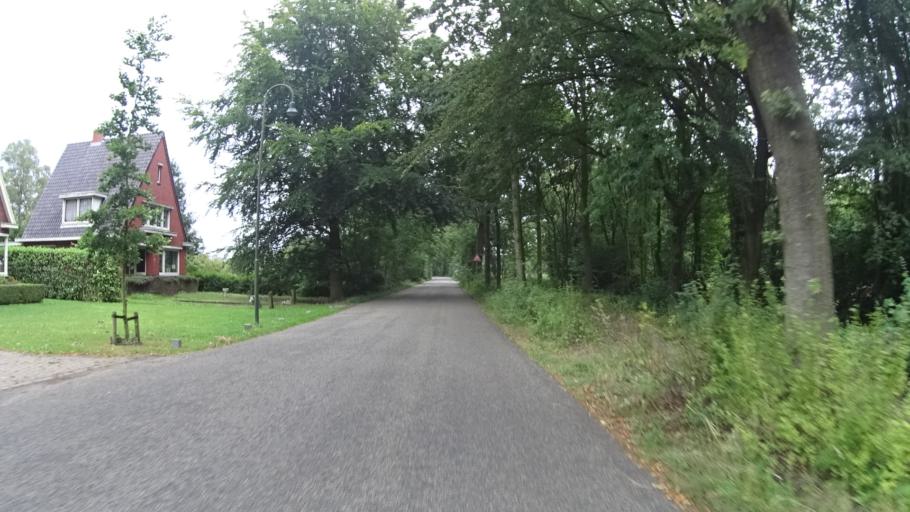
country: NL
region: Groningen
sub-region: Gemeente Slochteren
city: Slochteren
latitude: 53.2172
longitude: 6.8088
